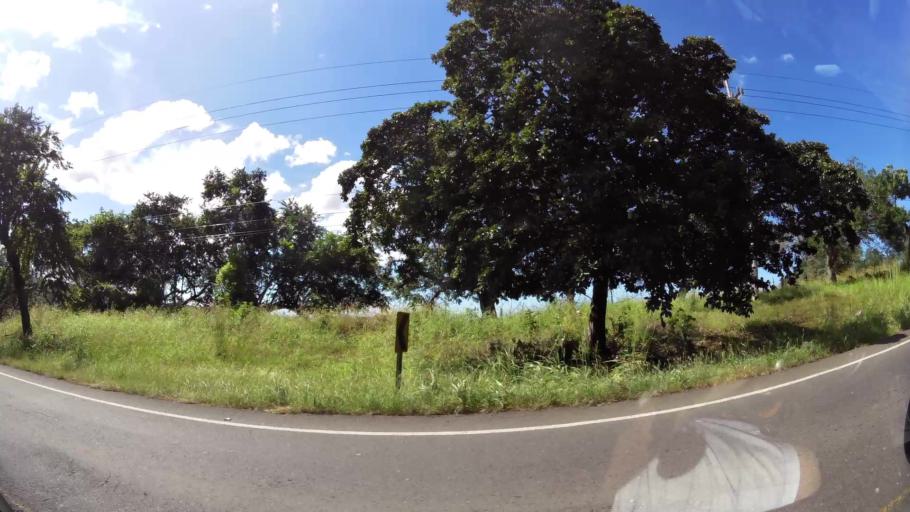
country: CR
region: Guanacaste
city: Juntas
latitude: 10.3241
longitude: -85.0501
